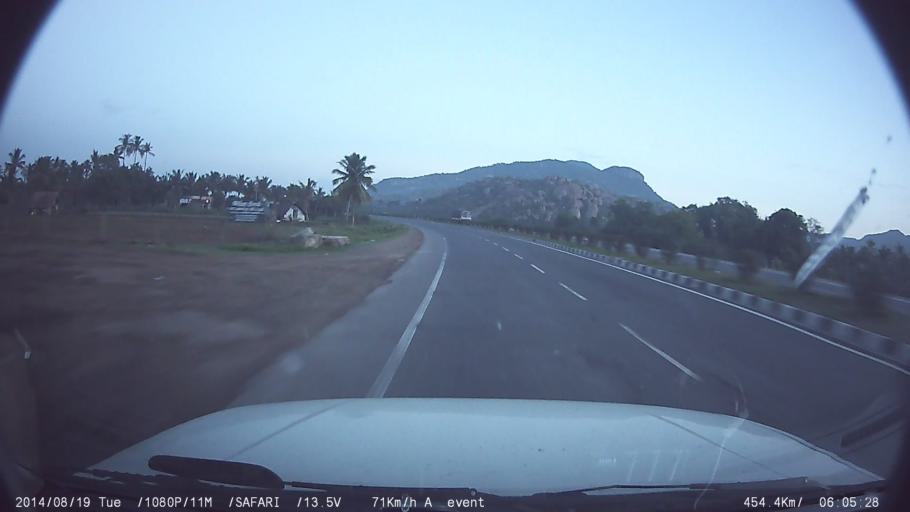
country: IN
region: Tamil Nadu
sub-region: Salem
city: Omalur
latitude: 11.8790
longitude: 78.0821
